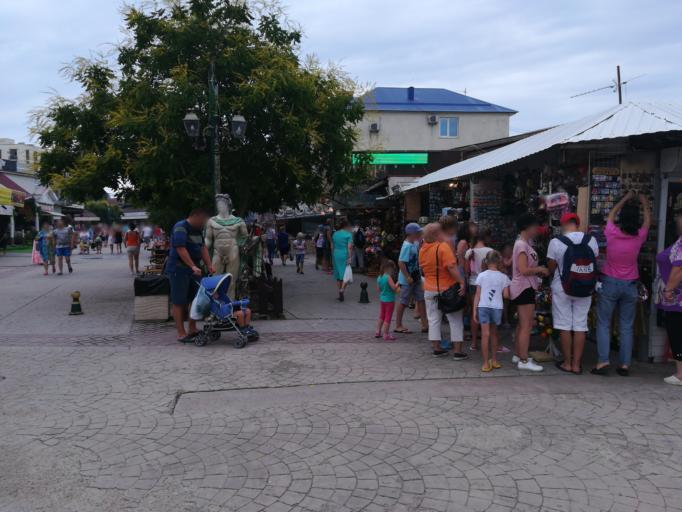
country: RU
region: Krasnodarskiy
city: Vityazevo
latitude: 44.9873
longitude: 37.2557
